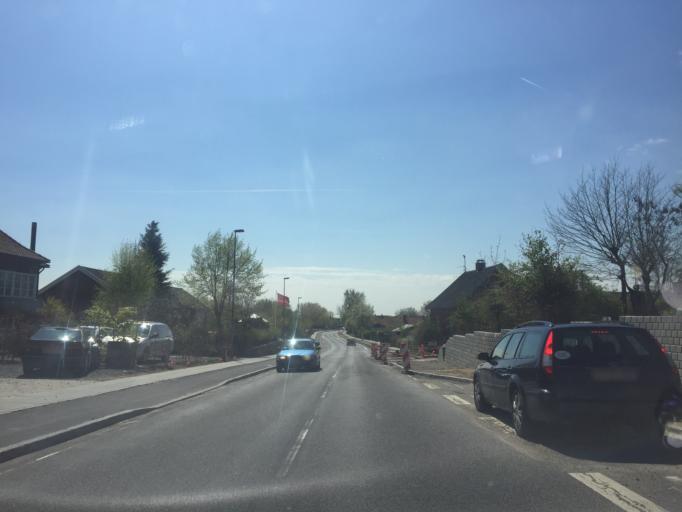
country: DK
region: Capital Region
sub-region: Allerod Kommune
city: Lynge
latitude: 55.8364
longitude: 12.2761
